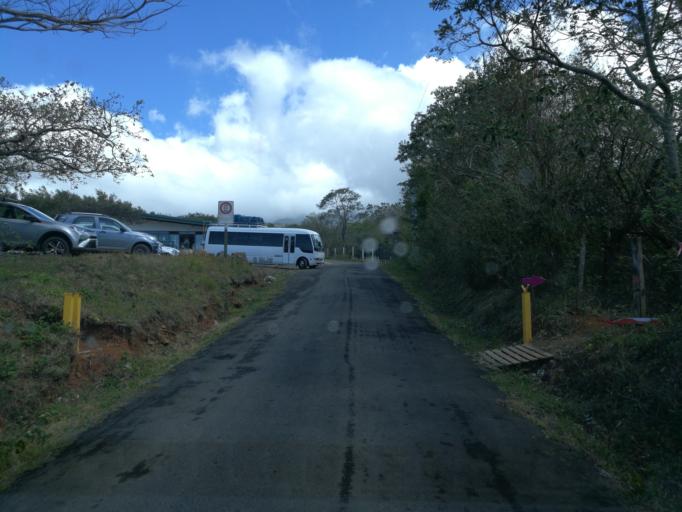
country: CR
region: Guanacaste
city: Liberia
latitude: 10.7725
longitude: -85.3498
